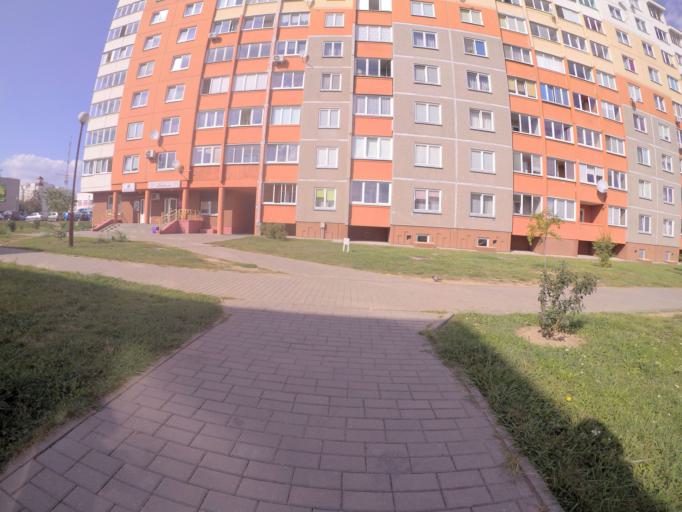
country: BY
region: Grodnenskaya
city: Hrodna
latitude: 53.6966
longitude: 23.8348
